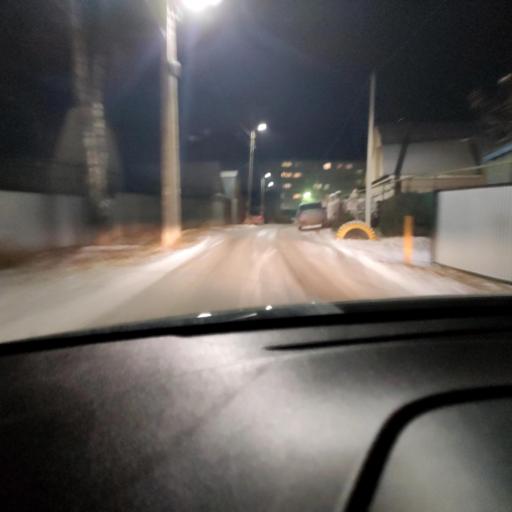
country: RU
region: Tatarstan
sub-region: Gorod Kazan'
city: Kazan
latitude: 55.7191
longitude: 49.0977
